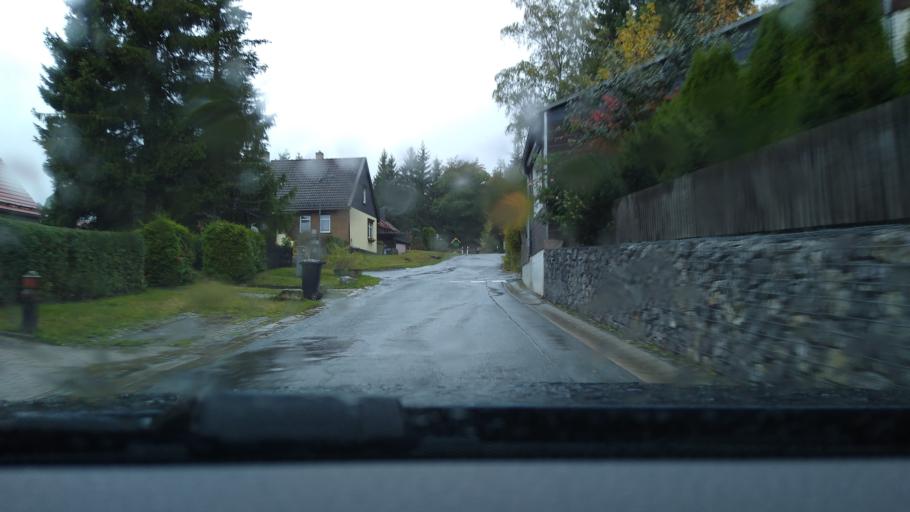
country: DE
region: Saxony-Anhalt
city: Benneckenstein
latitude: 51.6996
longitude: 10.7163
